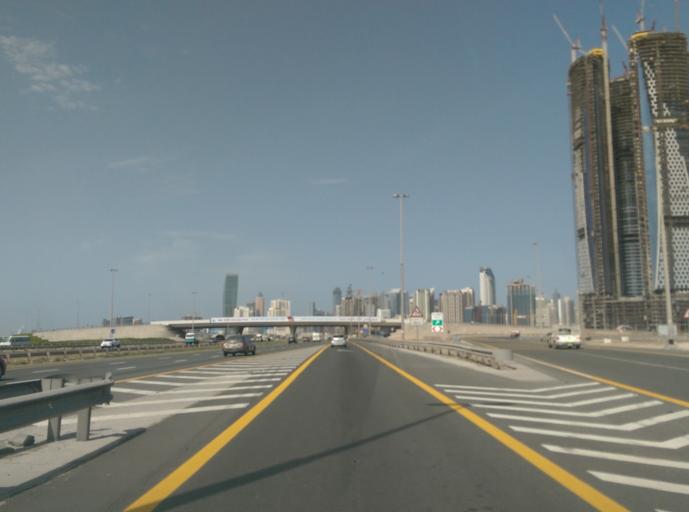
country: AE
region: Dubai
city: Dubai
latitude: 25.1833
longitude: 55.2967
